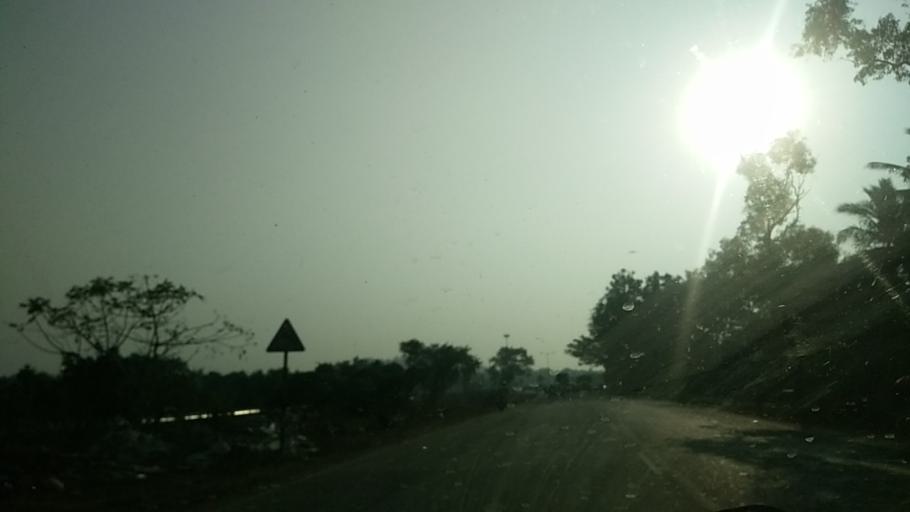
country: IN
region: Goa
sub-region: North Goa
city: Guirim
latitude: 15.5755
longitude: 73.8083
